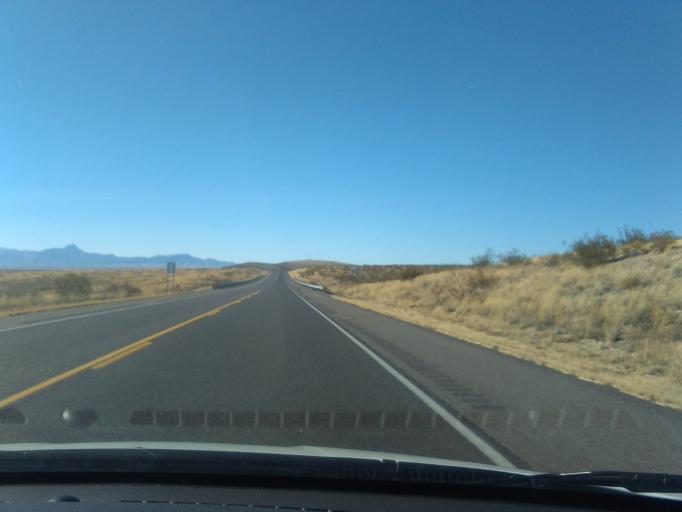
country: US
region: New Mexico
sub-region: Dona Ana County
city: Hatch
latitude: 32.5768
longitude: -107.4338
